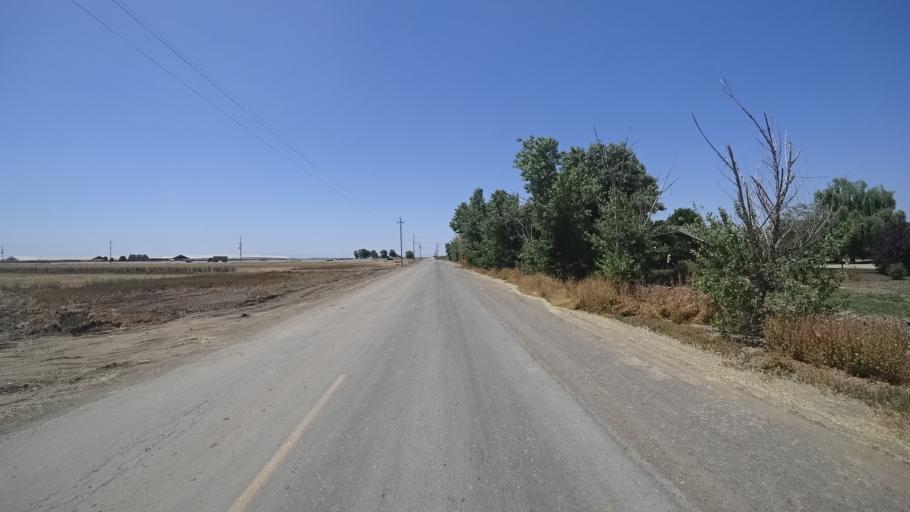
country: US
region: California
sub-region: Kings County
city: Home Garden
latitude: 36.1967
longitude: -119.6432
